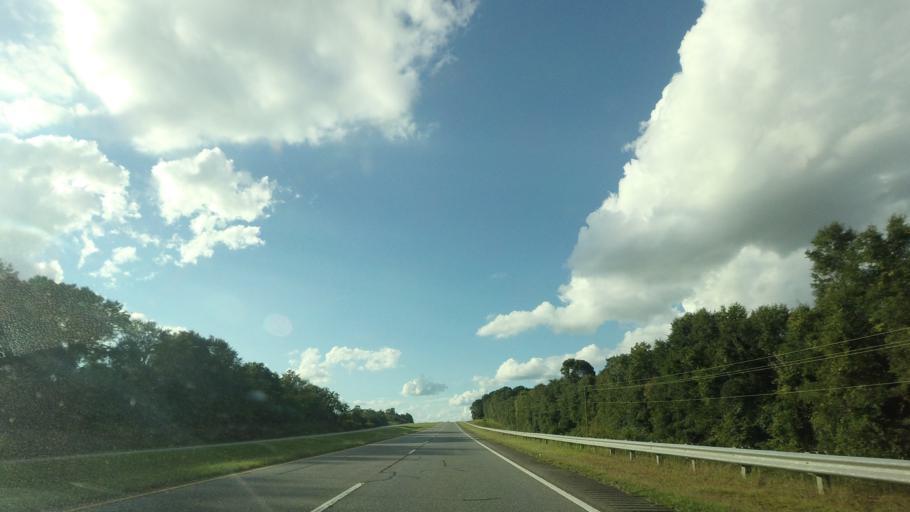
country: US
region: Georgia
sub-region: Houston County
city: Perry
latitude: 32.4360
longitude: -83.7242
